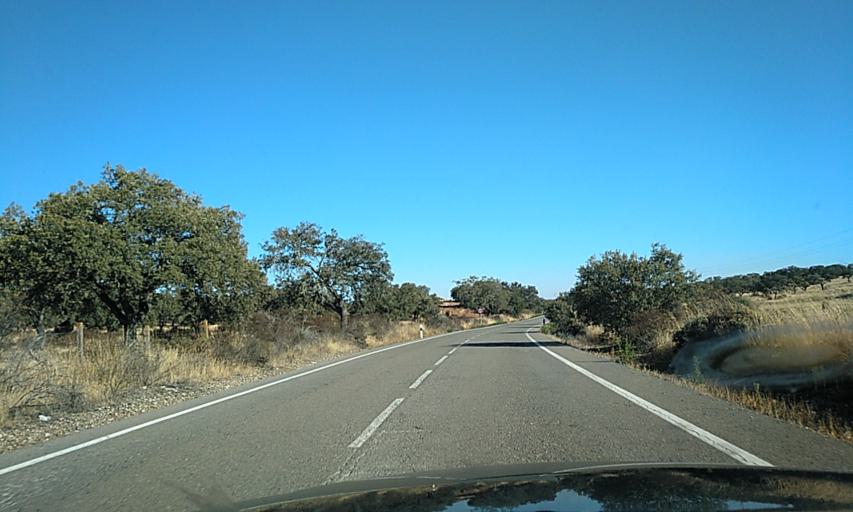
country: ES
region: Andalusia
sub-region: Provincia de Huelva
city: Santa Barbara de Casa
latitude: 37.7654
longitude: -7.1378
